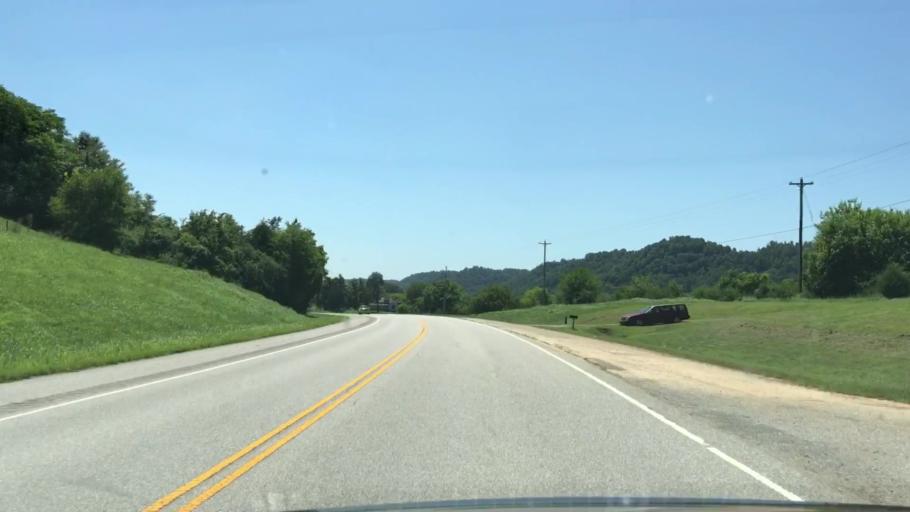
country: US
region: Tennessee
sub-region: Jackson County
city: Gainesboro
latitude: 36.4239
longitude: -85.6397
